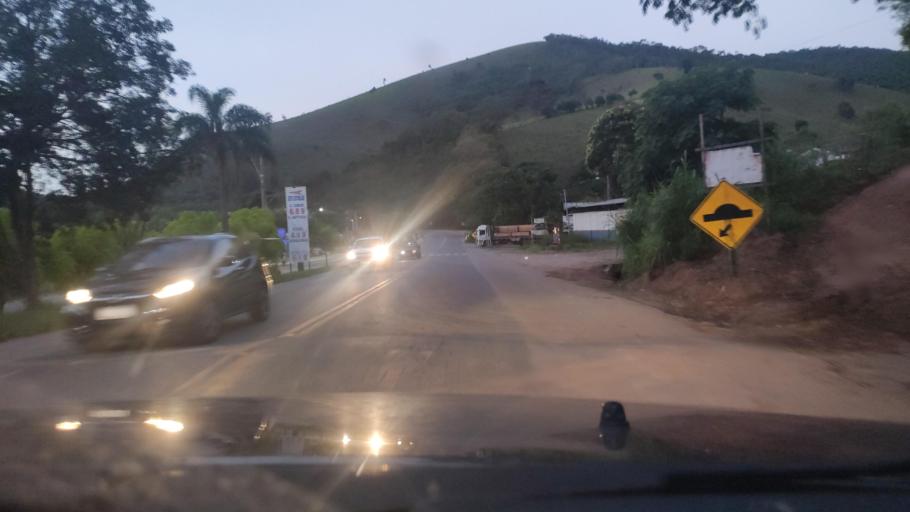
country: BR
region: Sao Paulo
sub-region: Campos Do Jordao
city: Campos do Jordao
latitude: -22.7443
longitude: -45.7396
